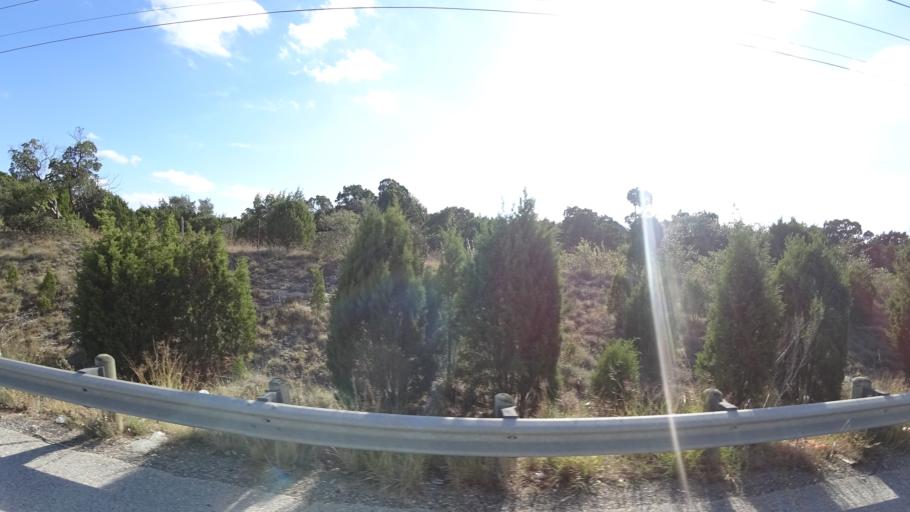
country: US
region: Texas
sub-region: Travis County
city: Barton Creek
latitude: 30.2565
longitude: -97.8797
